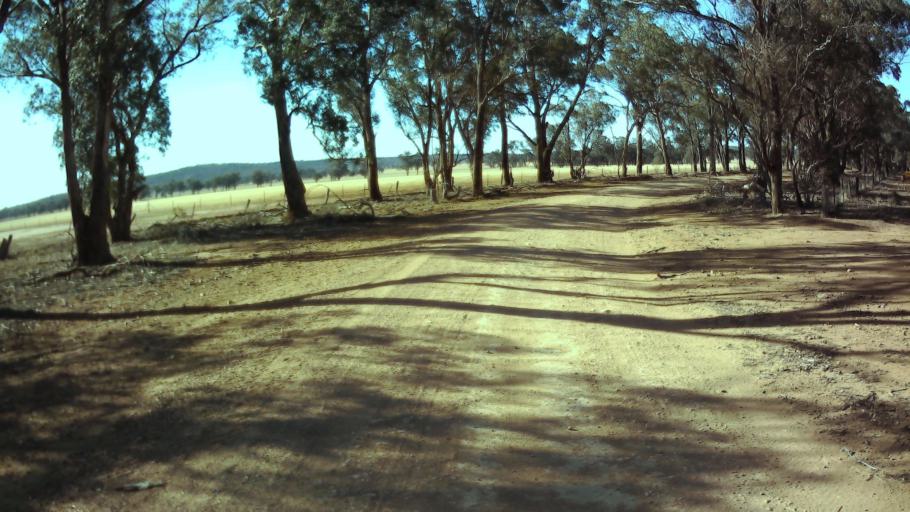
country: AU
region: New South Wales
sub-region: Weddin
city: Grenfell
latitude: -33.8356
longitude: 147.8729
